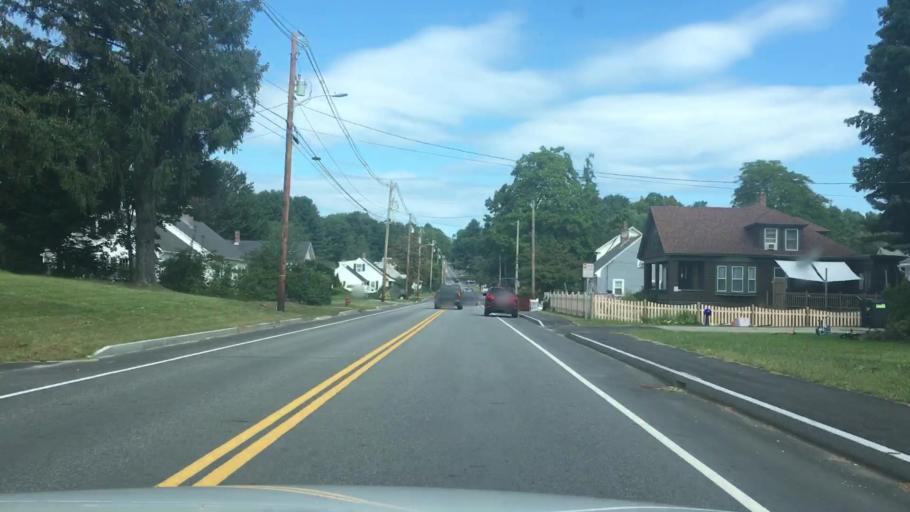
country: US
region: Maine
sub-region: Androscoggin County
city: Auburn
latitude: 44.1057
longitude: -70.2485
